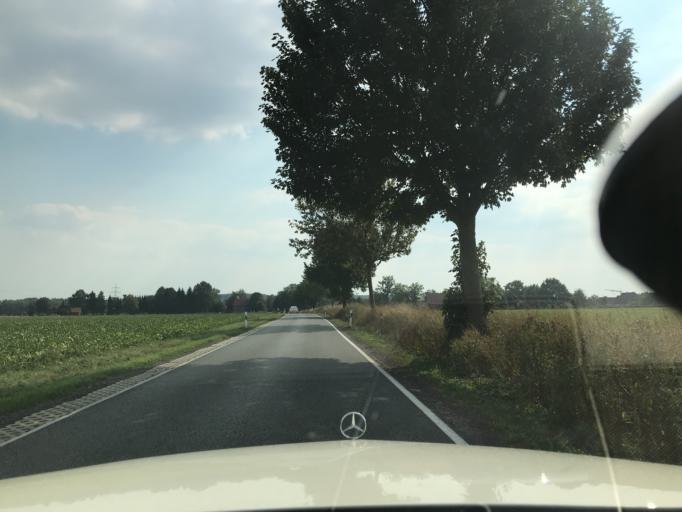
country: DE
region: North Rhine-Westphalia
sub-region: Regierungsbezirk Arnsberg
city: Werl
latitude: 51.6067
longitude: 7.8749
